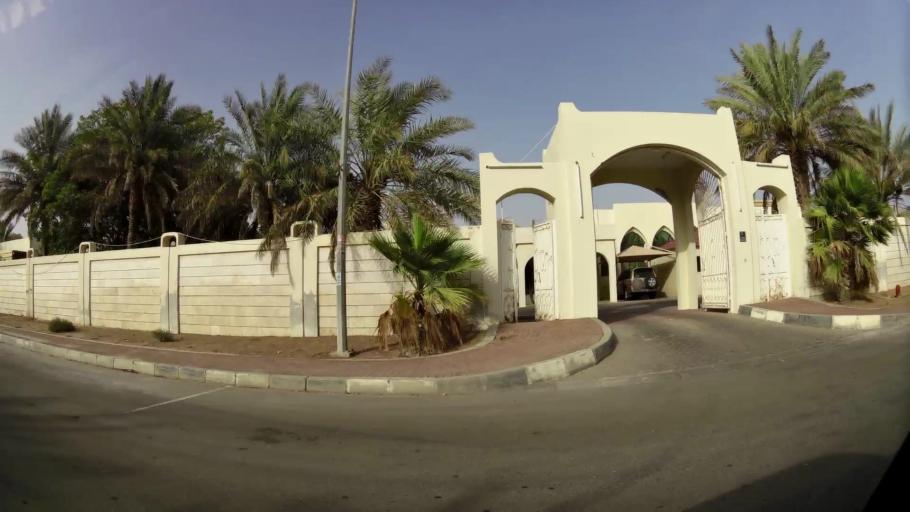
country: AE
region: Abu Dhabi
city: Al Ain
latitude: 24.2177
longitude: 55.6505
